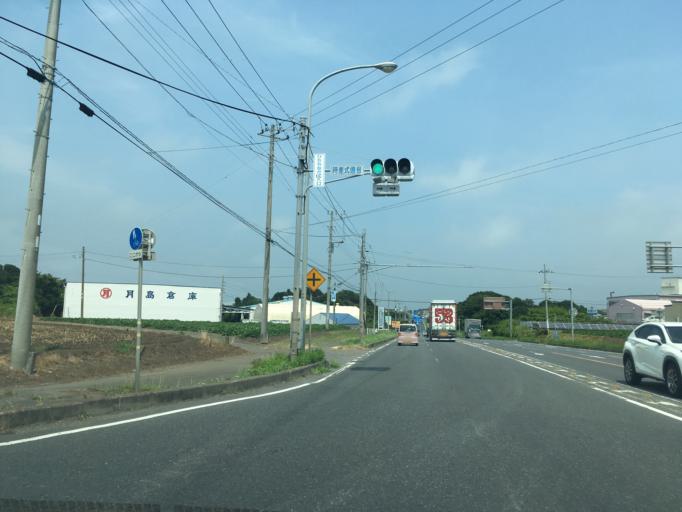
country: JP
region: Ibaraki
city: Katsuta
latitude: 36.3731
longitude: 140.5786
